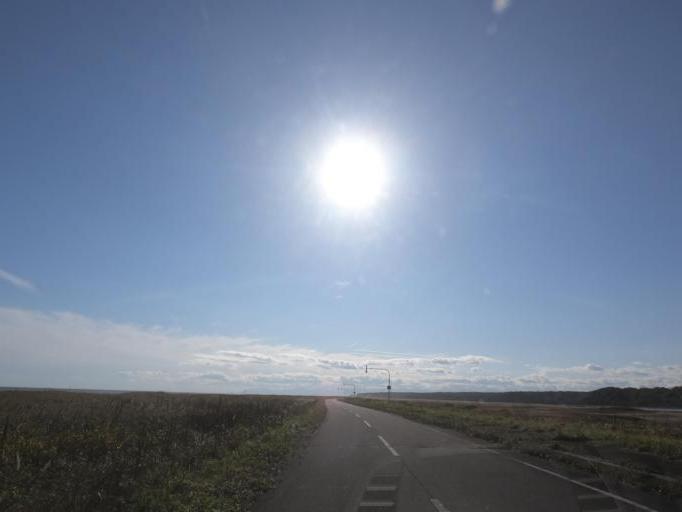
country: JP
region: Hokkaido
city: Obihiro
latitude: 42.5959
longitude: 143.5457
